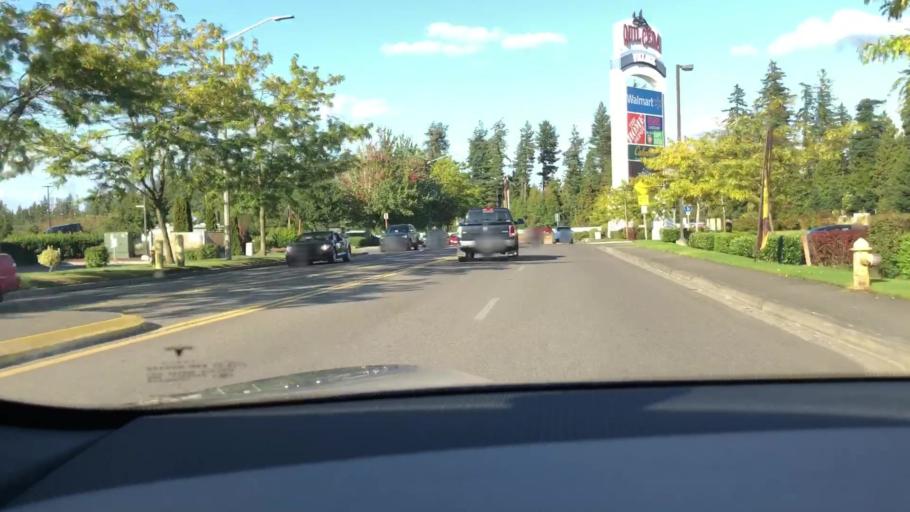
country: US
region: Washington
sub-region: Snohomish County
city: Marysville
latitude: 48.0773
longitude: -122.1869
